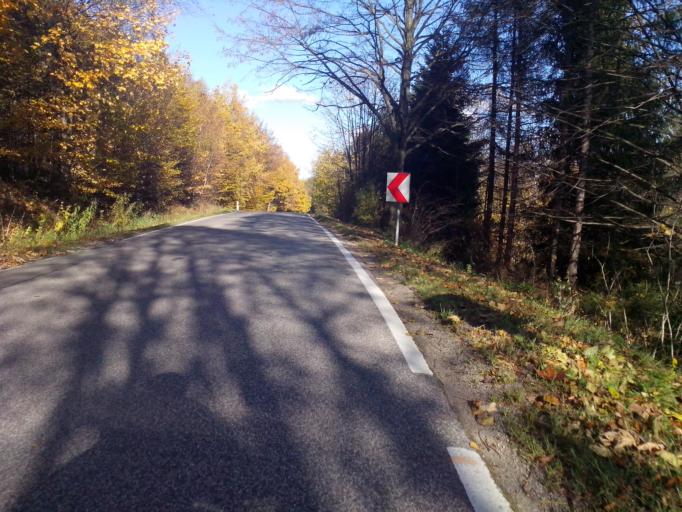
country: PL
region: Subcarpathian Voivodeship
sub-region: Powiat krosnienski
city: Korczyna
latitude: 49.7683
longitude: 21.8465
